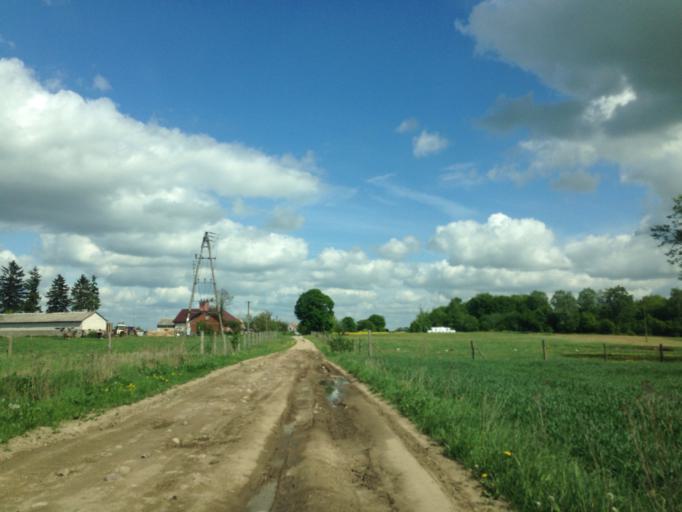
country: PL
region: Warmian-Masurian Voivodeship
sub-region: Powiat ostrodzki
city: Dabrowno
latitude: 53.3961
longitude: 20.1554
